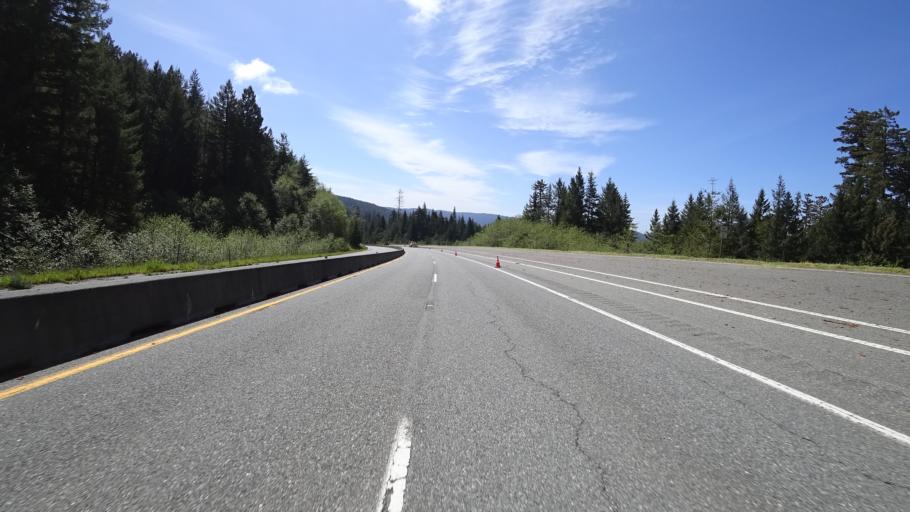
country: US
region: California
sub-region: Humboldt County
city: Westhaven-Moonstone
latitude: 41.3776
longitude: -123.9950
